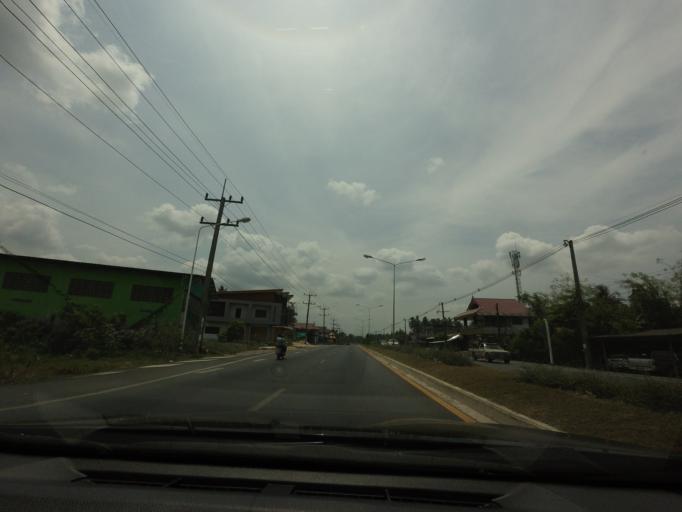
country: TH
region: Yala
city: Yala
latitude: 6.5042
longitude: 101.2837
